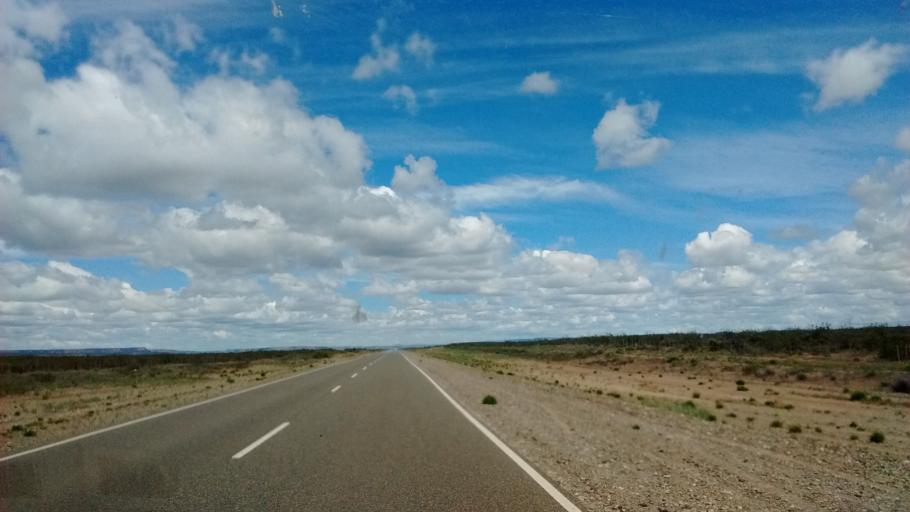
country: AR
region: Neuquen
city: Piedra del Aguila
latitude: -39.8283
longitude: -69.7514
